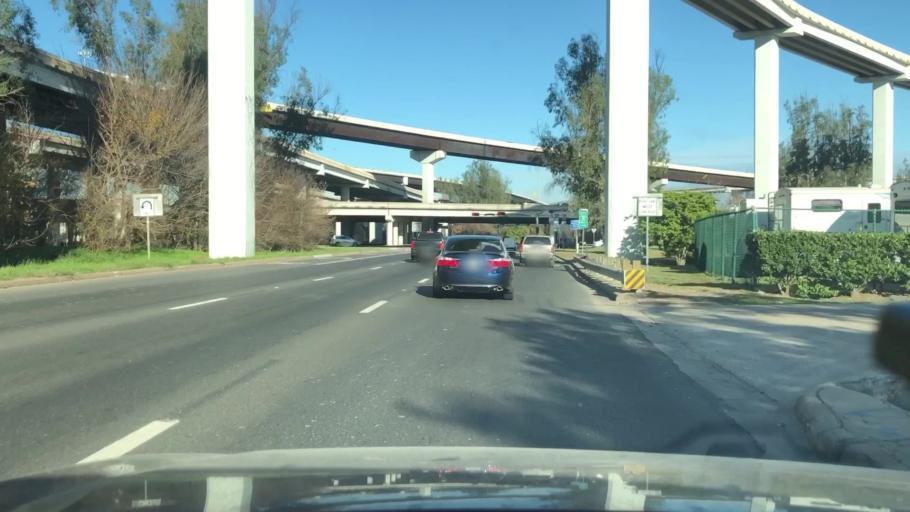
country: US
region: Texas
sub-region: Fort Bend County
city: Meadows Place
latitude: 29.6600
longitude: -95.5565
